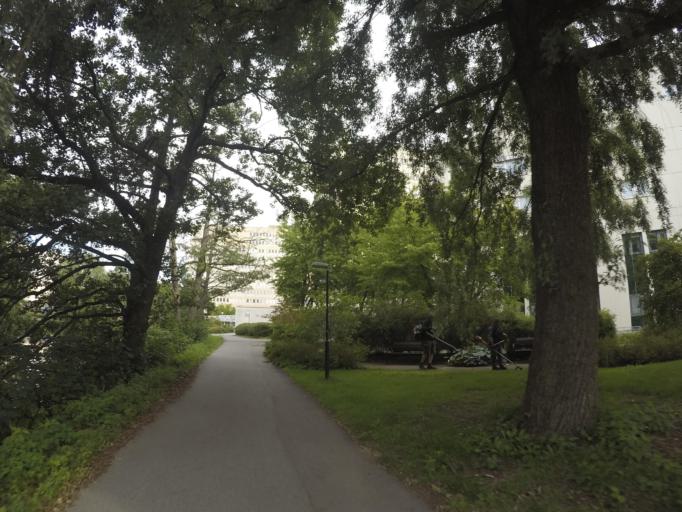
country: SE
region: OErebro
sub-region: Orebro Kommun
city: Orebro
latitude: 59.2747
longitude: 15.2275
